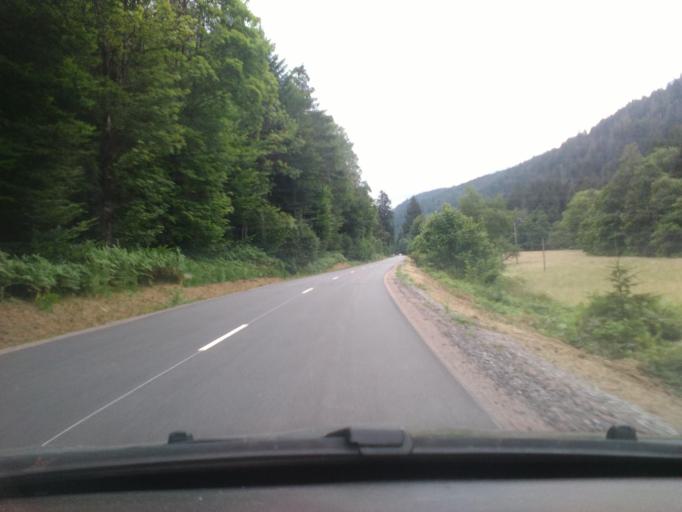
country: FR
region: Lorraine
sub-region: Departement des Vosges
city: Granges-sur-Vologne
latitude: 48.1225
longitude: 6.8385
